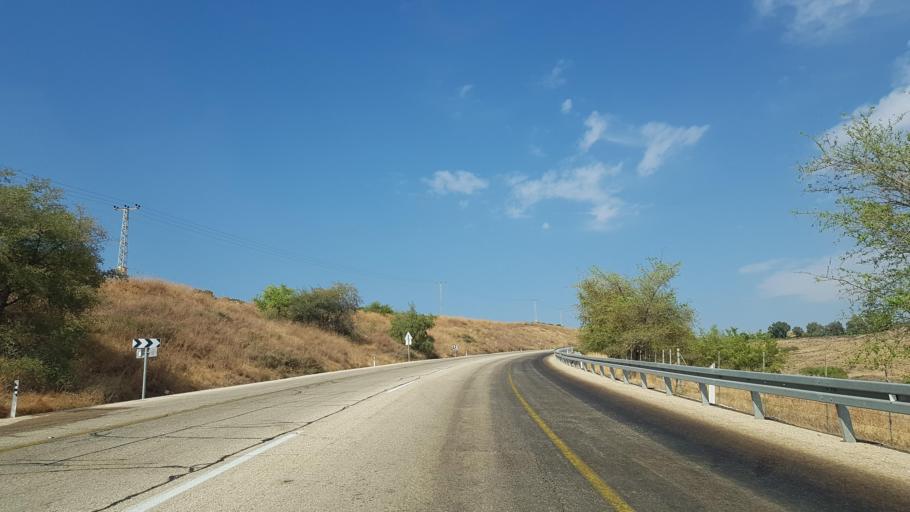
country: SY
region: Quneitra
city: Al Butayhah
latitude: 32.8992
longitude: 35.5965
